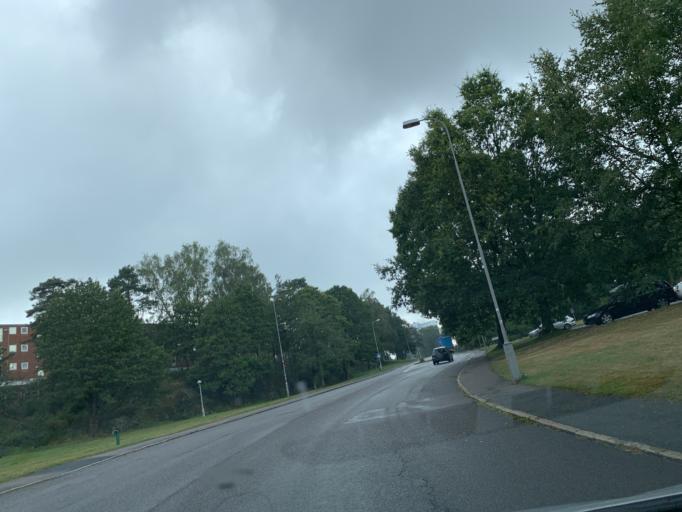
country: SE
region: Vaestra Goetaland
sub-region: Goteborg
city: Eriksbo
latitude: 57.7477
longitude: 12.0277
